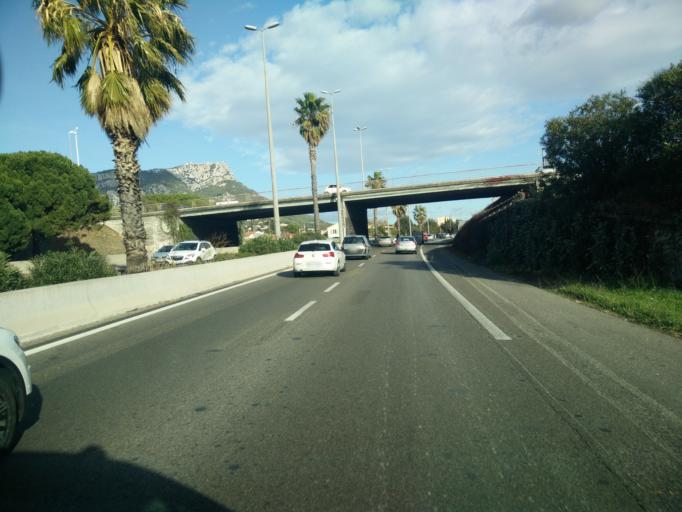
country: FR
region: Provence-Alpes-Cote d'Azur
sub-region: Departement du Var
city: La Valette-du-Var
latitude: 43.1321
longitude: 5.9811
